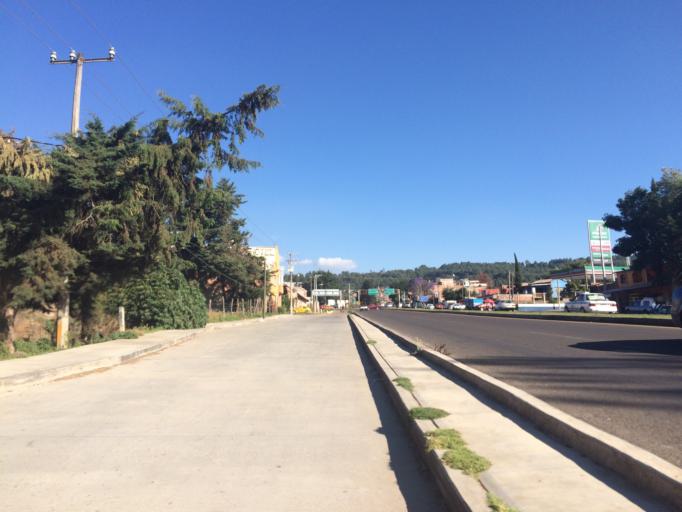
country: MX
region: Michoacan
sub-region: Patzcuaro
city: Colonia Vista Bella (Lomas del Peaje)
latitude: 19.4983
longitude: -101.6003
